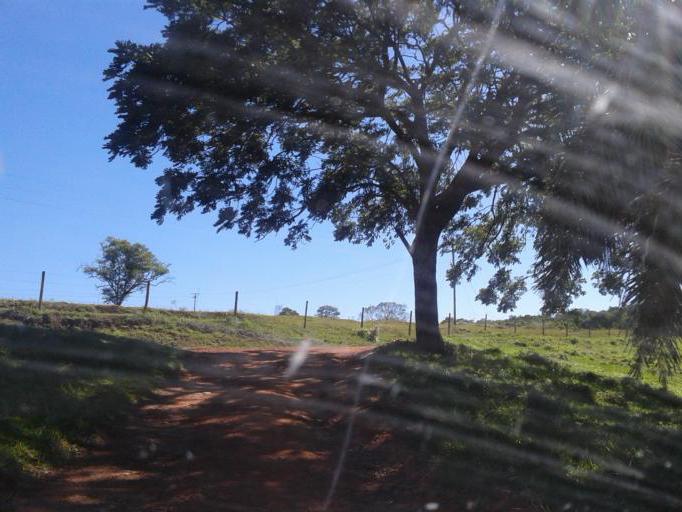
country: BR
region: Minas Gerais
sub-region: Capinopolis
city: Capinopolis
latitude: -18.6743
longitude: -49.5652
